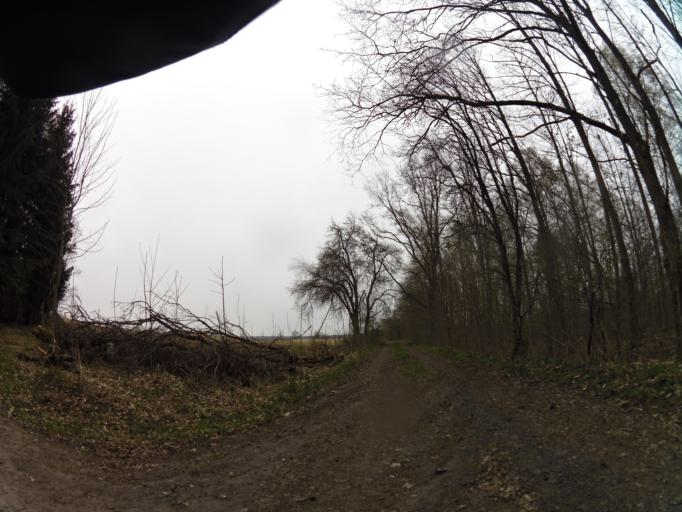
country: PL
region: West Pomeranian Voivodeship
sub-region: Powiat koszalinski
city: Bobolice
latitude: 53.9861
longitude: 16.6534
